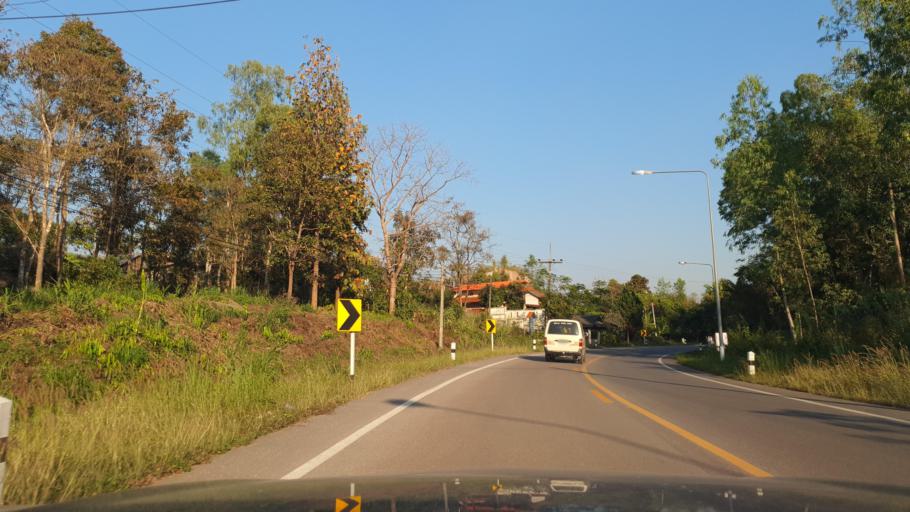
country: TH
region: Chiang Rai
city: Mae Lao
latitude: 19.8337
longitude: 99.6848
